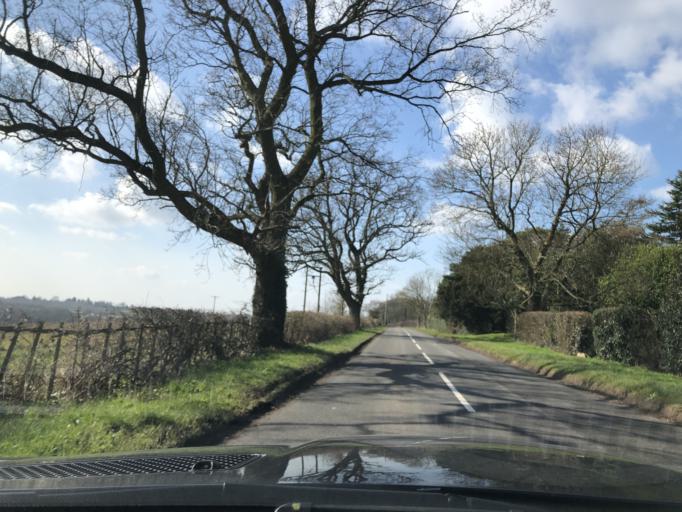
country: GB
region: England
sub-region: Warwickshire
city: Harbury
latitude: 52.2861
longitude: -1.4719
